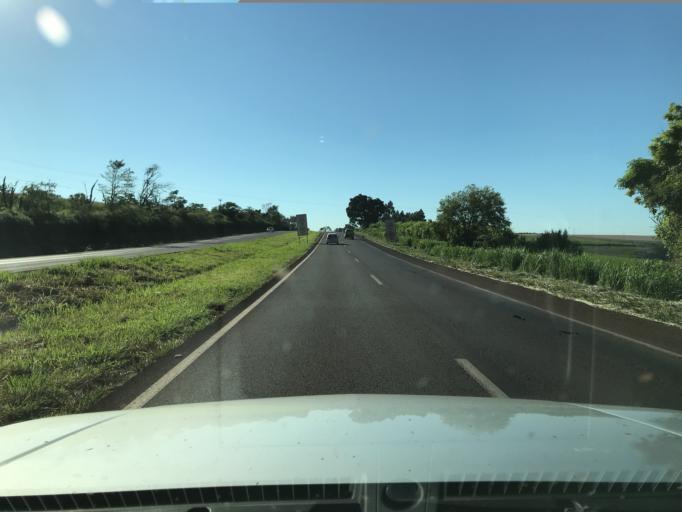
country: BR
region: Parana
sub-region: Cascavel
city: Cascavel
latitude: -24.8891
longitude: -53.5533
